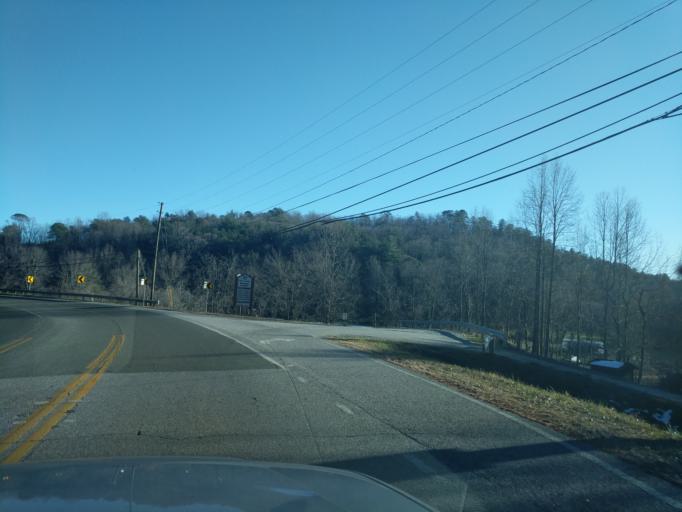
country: US
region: Georgia
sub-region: Rabun County
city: Clayton
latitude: 34.8804
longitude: -83.4099
